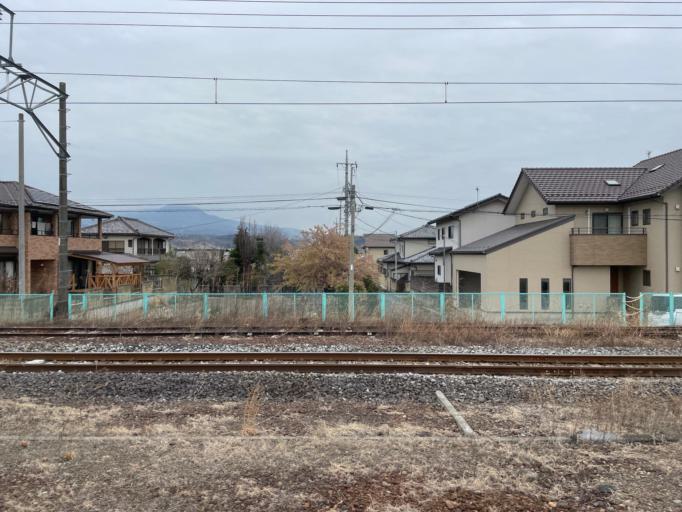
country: JP
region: Gunma
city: Shibukawa
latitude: 36.4624
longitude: 139.0195
